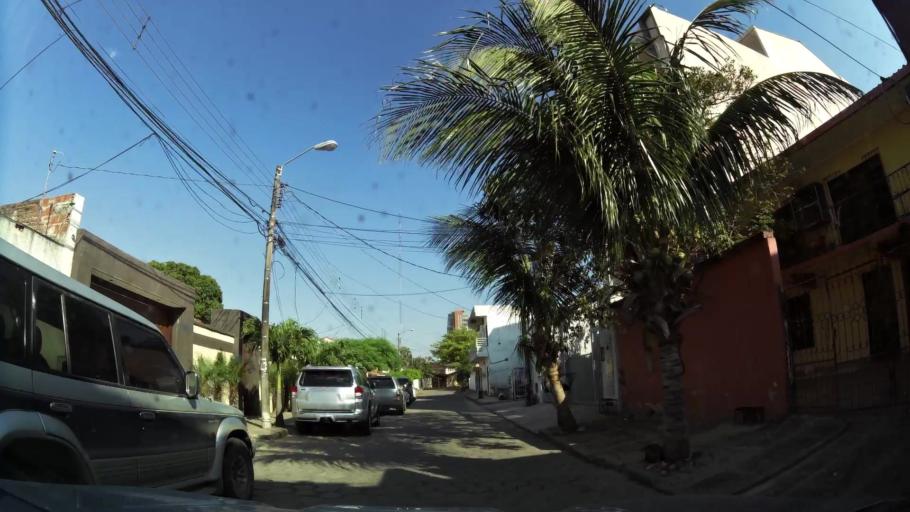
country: BO
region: Santa Cruz
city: Santa Cruz de la Sierra
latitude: -17.7765
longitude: -63.1698
